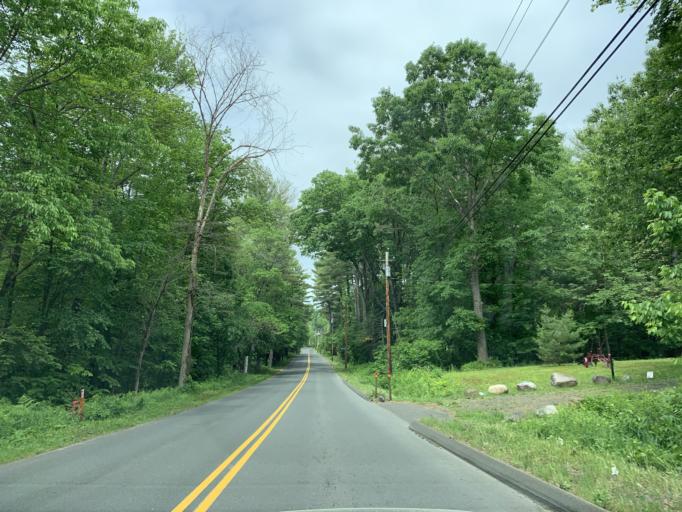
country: US
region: Massachusetts
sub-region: Hampshire County
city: Southampton
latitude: 42.1833
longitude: -72.7283
